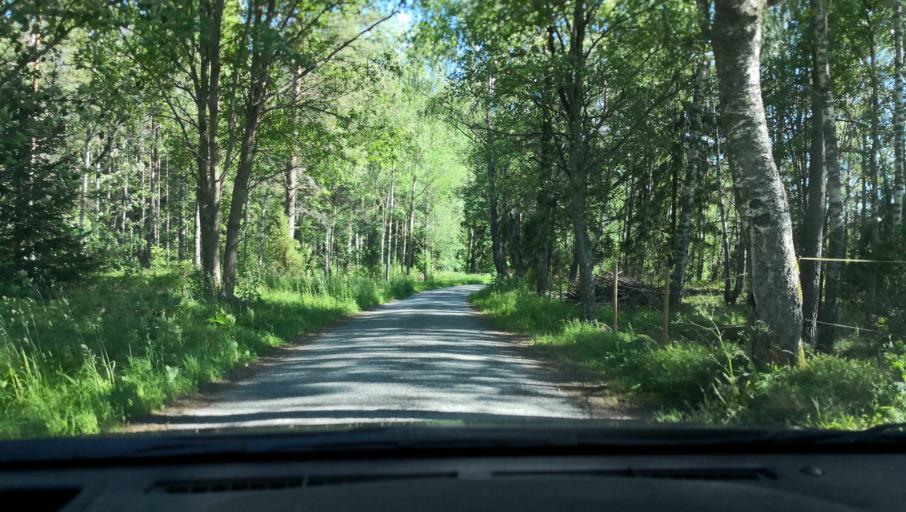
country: SE
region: Soedermanland
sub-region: Eskilstuna Kommun
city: Arla
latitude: 59.3275
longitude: 16.5962
